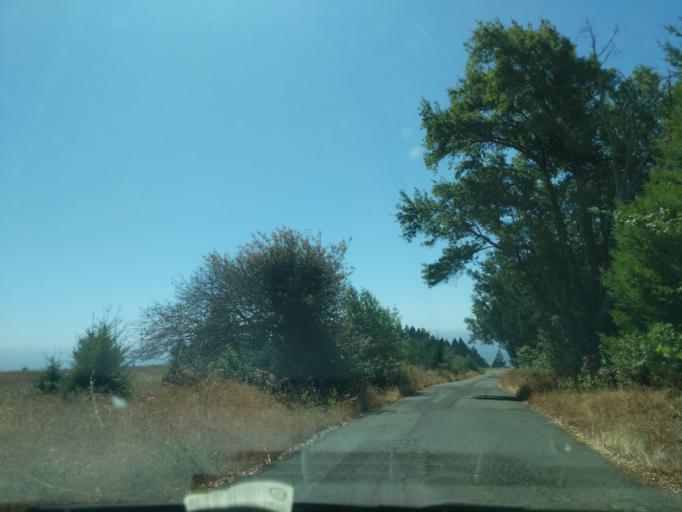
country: US
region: California
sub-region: Sonoma County
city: Monte Rio
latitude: 38.5305
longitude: -123.2250
